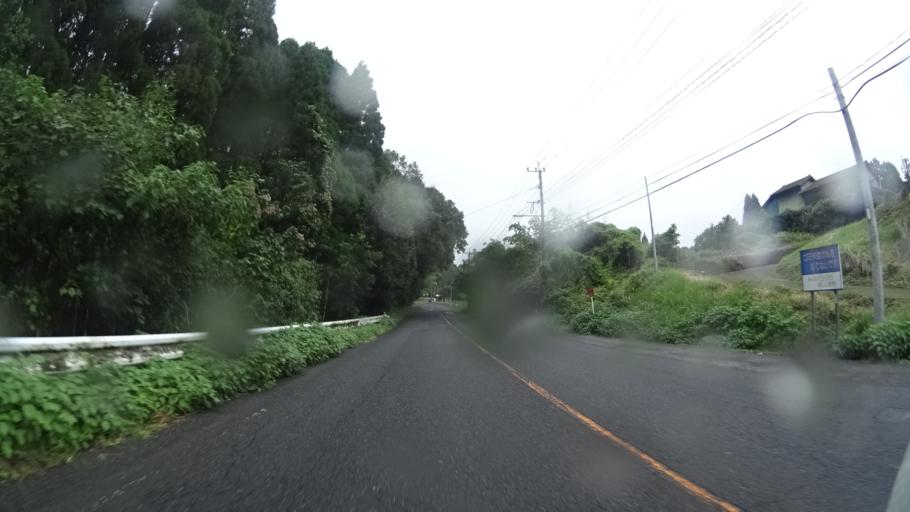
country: JP
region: Kagoshima
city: Kajiki
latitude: 31.7894
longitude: 130.6759
